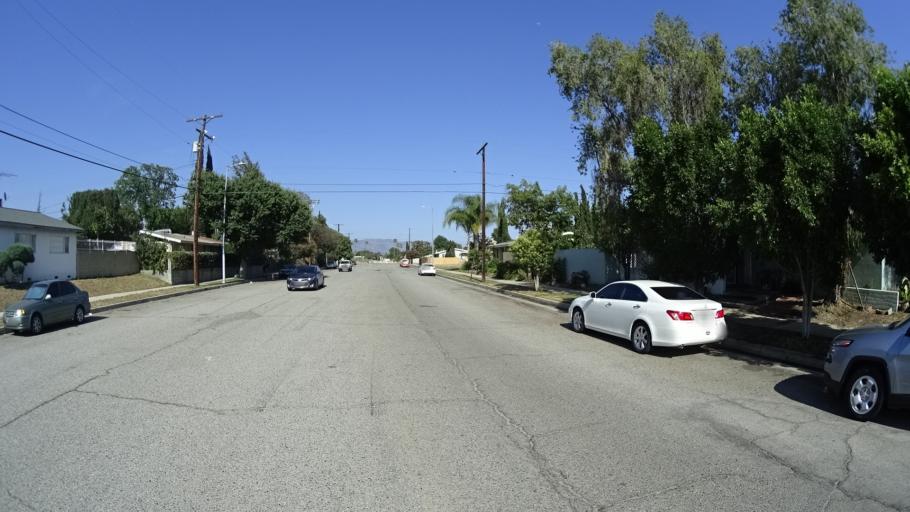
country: US
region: California
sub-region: Los Angeles County
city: Van Nuys
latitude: 34.2159
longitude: -118.4266
